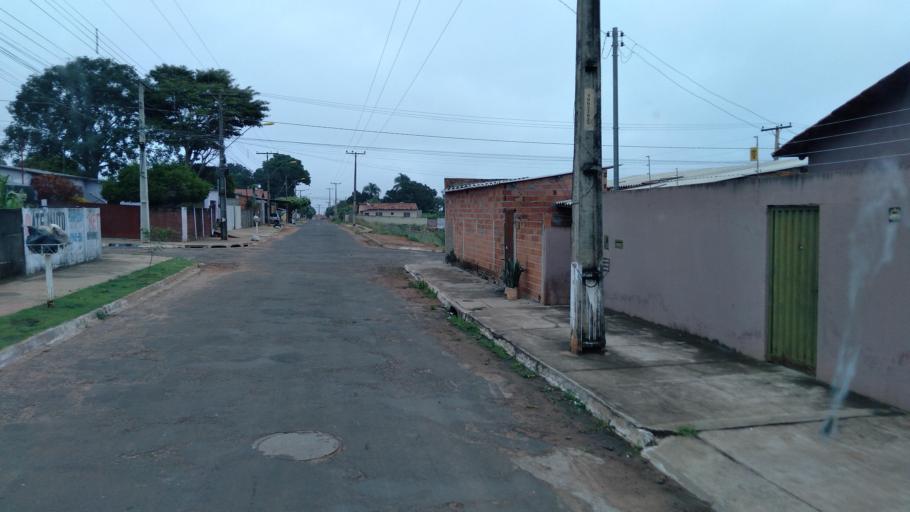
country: BR
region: Goias
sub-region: Mineiros
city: Mineiros
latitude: -17.5791
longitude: -52.5456
